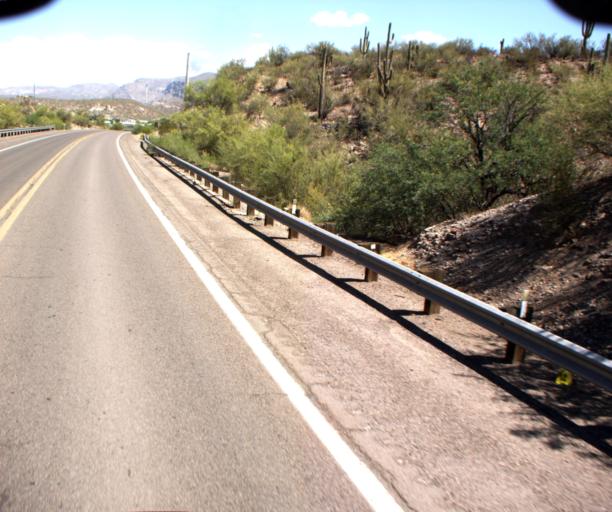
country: US
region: Arizona
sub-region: Pinal County
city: Kearny
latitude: 32.9788
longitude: -110.7687
